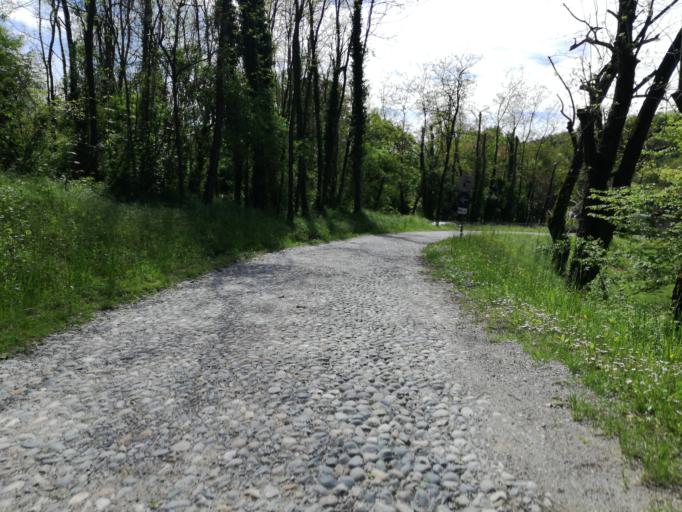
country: IT
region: Lombardy
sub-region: Provincia di Monza e Brianza
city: Porto d'Adda
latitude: 45.6546
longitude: 9.4846
